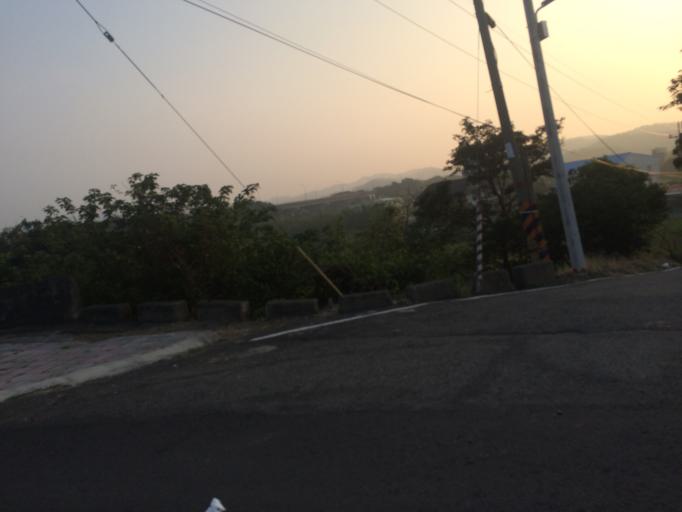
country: TW
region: Taiwan
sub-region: Hsinchu
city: Hsinchu
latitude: 24.7383
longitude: 120.9107
